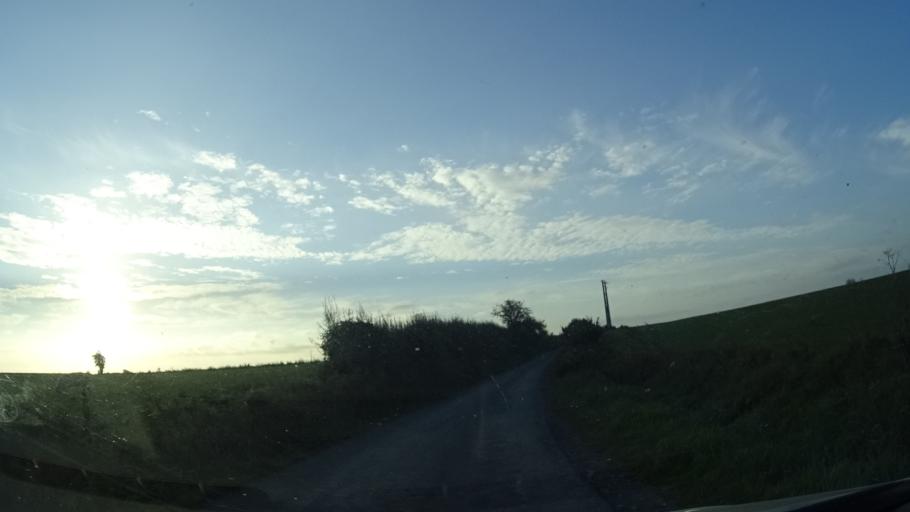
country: BE
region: Wallonia
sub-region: Province du Hainaut
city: Beaumont
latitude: 50.2410
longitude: 4.2686
